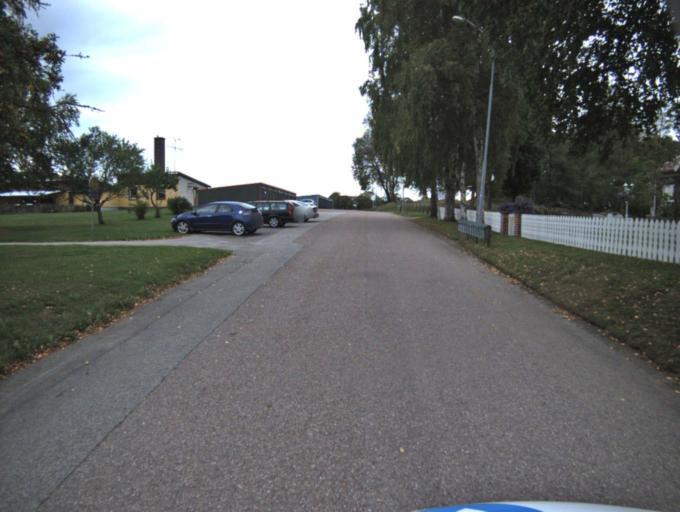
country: SE
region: Vaestra Goetaland
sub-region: Ulricehamns Kommun
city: Ulricehamn
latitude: 57.8430
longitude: 13.2823
